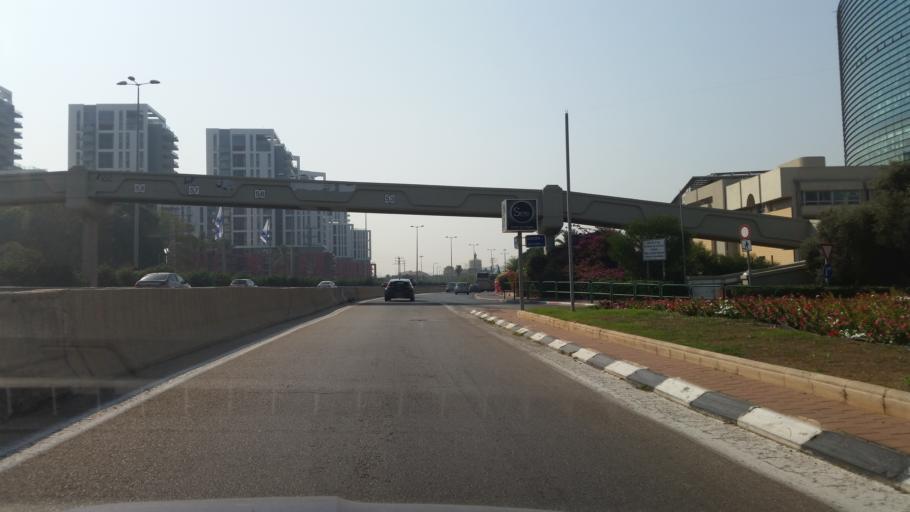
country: IL
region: Tel Aviv
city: Herzliyya
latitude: 32.1653
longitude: 34.8134
